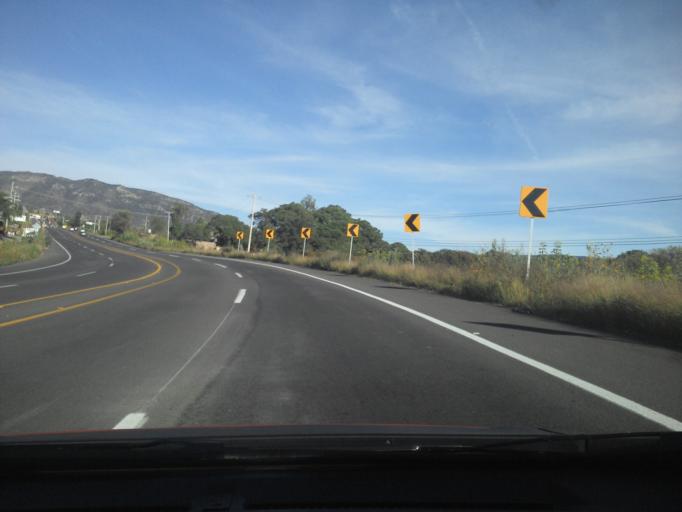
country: MX
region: Jalisco
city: La Venta del Astillero
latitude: 20.7276
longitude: -103.6162
